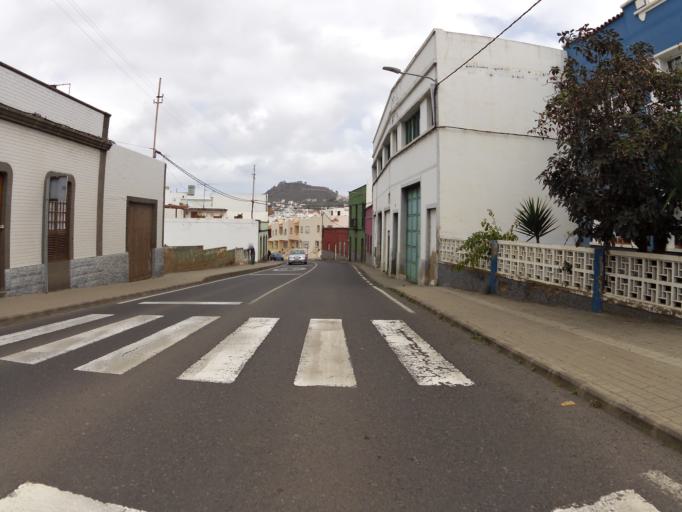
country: ES
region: Canary Islands
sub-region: Provincia de Las Palmas
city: Arucas
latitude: 28.1084
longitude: -15.5260
